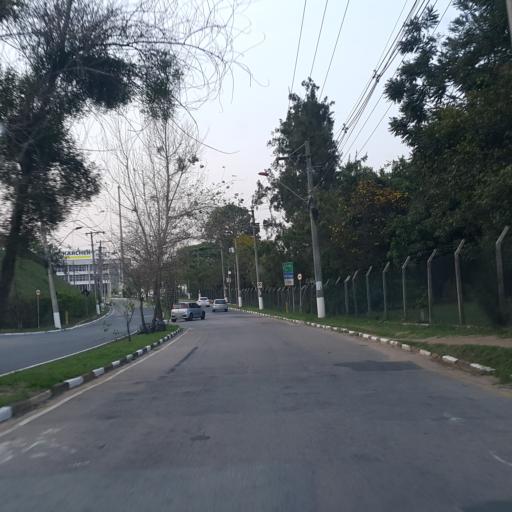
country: BR
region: Sao Paulo
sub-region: Vinhedo
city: Vinhedo
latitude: -23.0639
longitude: -46.9993
